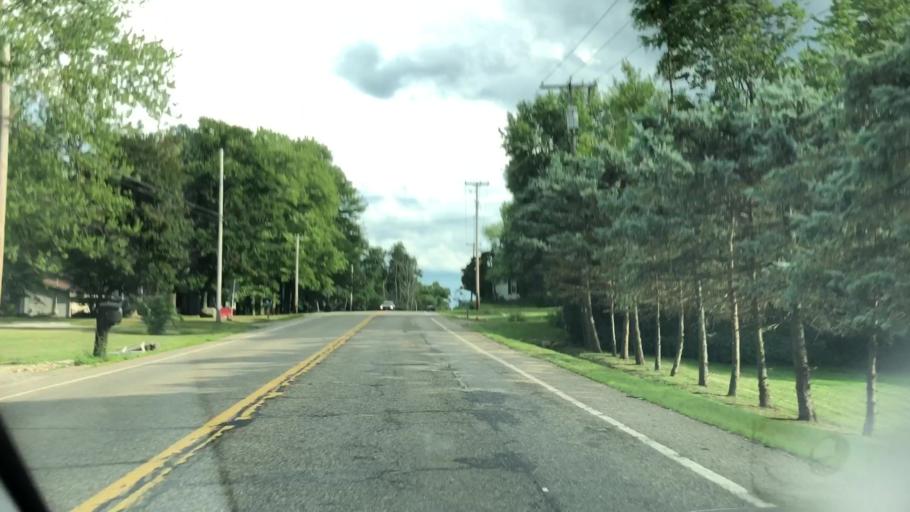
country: US
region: Ohio
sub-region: Summit County
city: Greensburg
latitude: 40.9222
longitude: -81.4633
